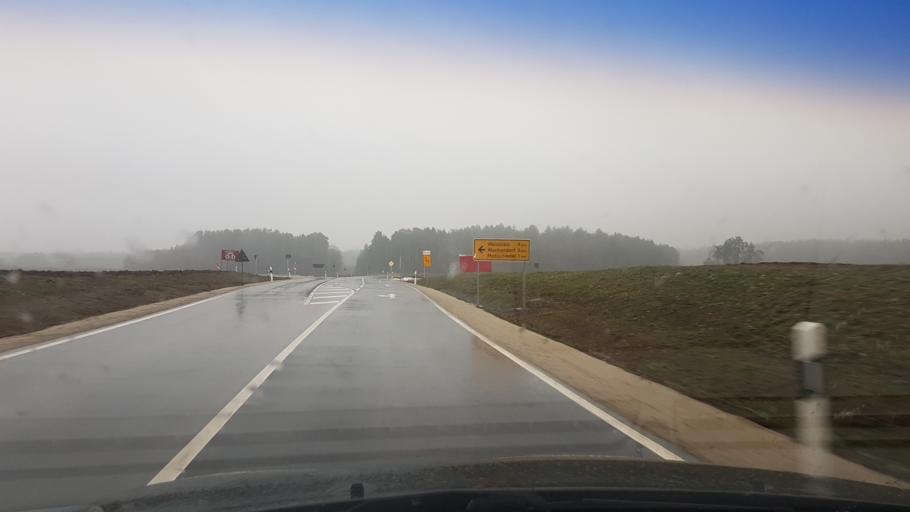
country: DE
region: Bavaria
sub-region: Upper Franconia
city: Wonsees
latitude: 50.0236
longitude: 11.2665
